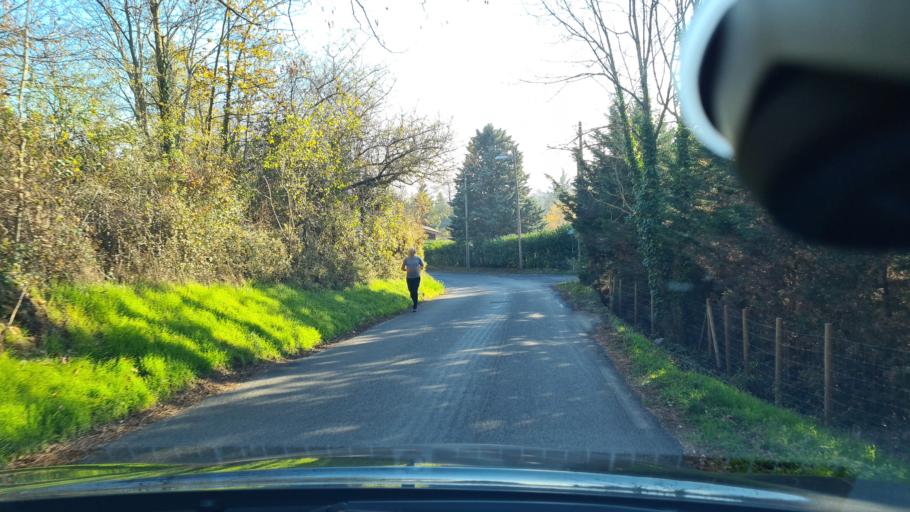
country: FR
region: Rhone-Alpes
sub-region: Departement du Rhone
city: Limonest
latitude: 45.8287
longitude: 4.8095
